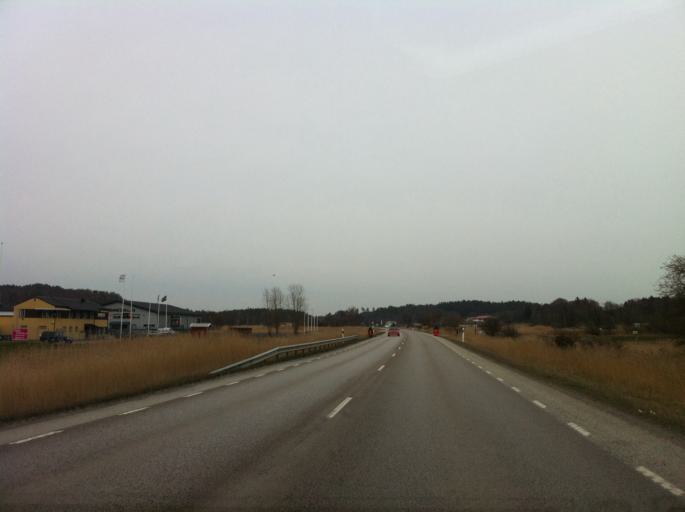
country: SE
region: Vaestra Goetaland
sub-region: Tjorns Kommun
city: Myggenas
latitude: 58.0234
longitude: 11.6965
